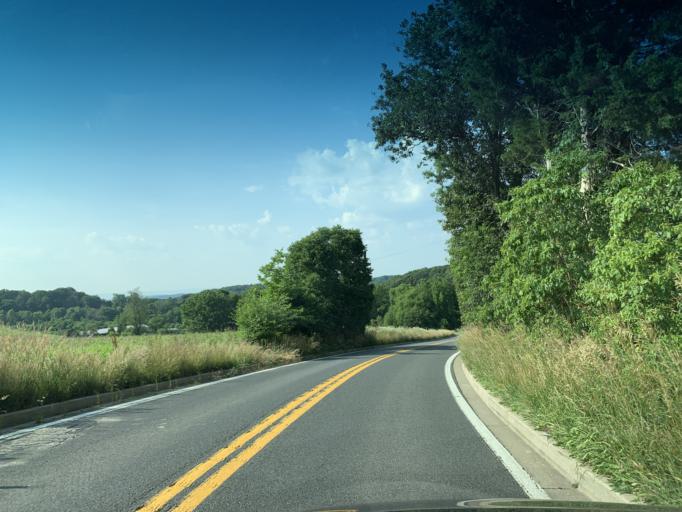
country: US
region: Maryland
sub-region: Montgomery County
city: Clarksburg
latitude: 39.2545
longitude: -77.3463
